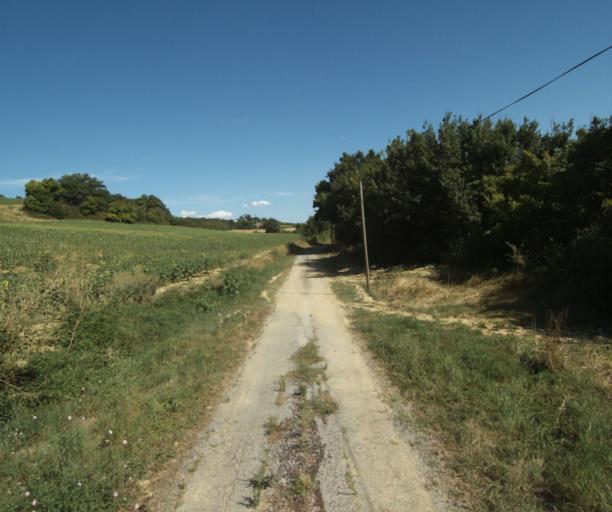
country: FR
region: Midi-Pyrenees
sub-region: Departement de la Haute-Garonne
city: Saint-Felix-Lauragais
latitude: 43.5216
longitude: 1.9061
